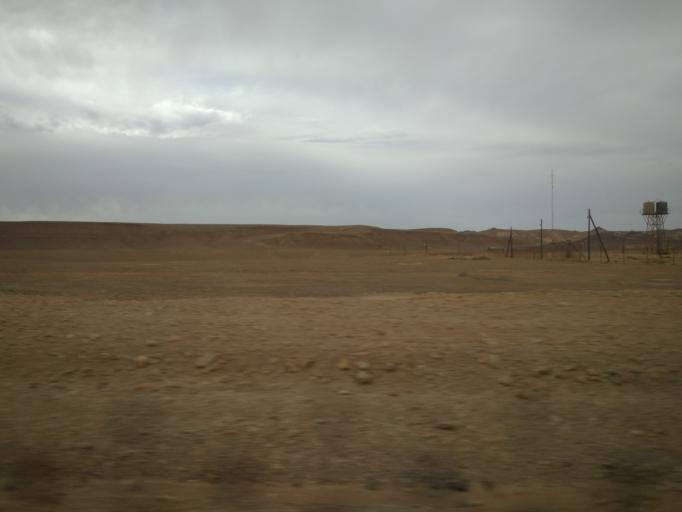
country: IL
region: Southern District
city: Eilat
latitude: 29.8572
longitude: 34.8446
